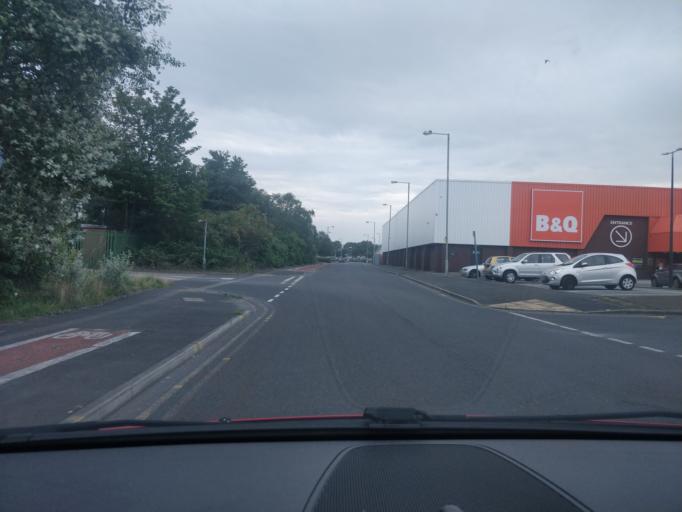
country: GB
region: England
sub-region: Sefton
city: Southport
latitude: 53.6338
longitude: -2.9680
